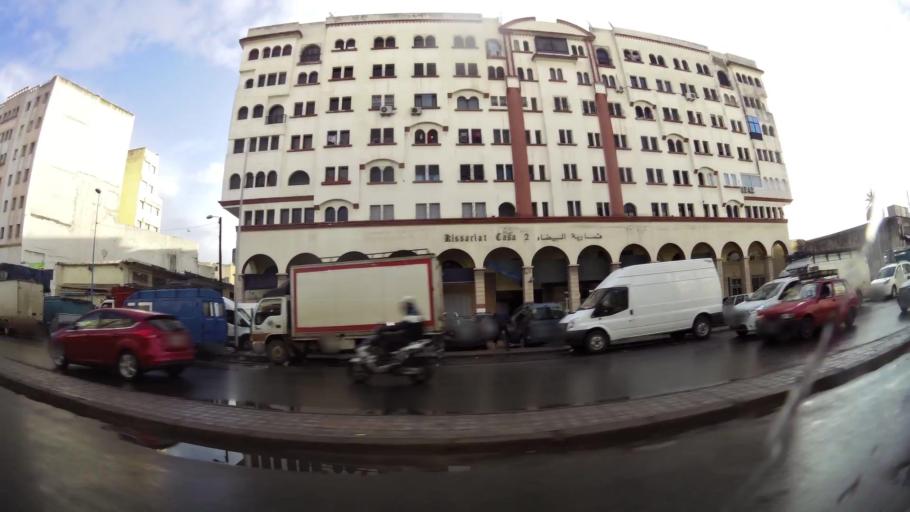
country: MA
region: Grand Casablanca
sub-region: Casablanca
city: Casablanca
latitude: 33.5872
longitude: -7.6080
